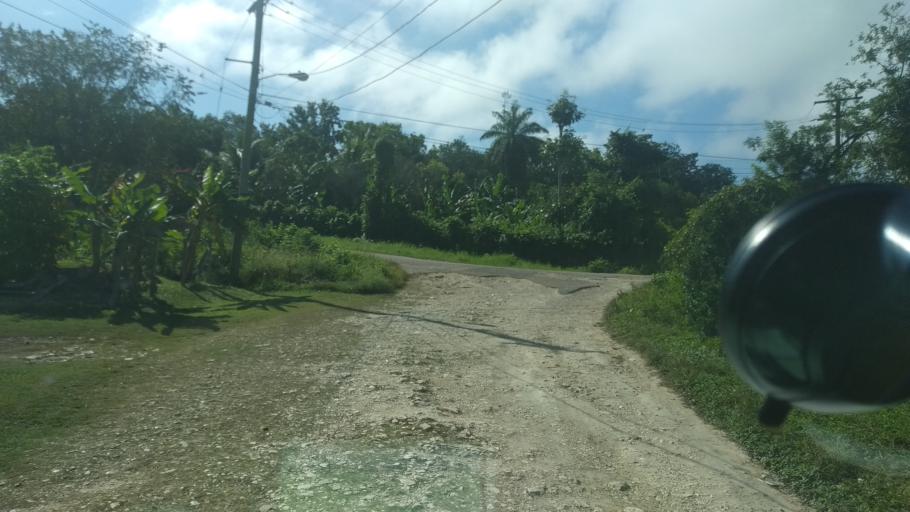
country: BZ
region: Cayo
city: Benque Viejo del Carmen
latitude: 17.0843
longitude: -89.1323
